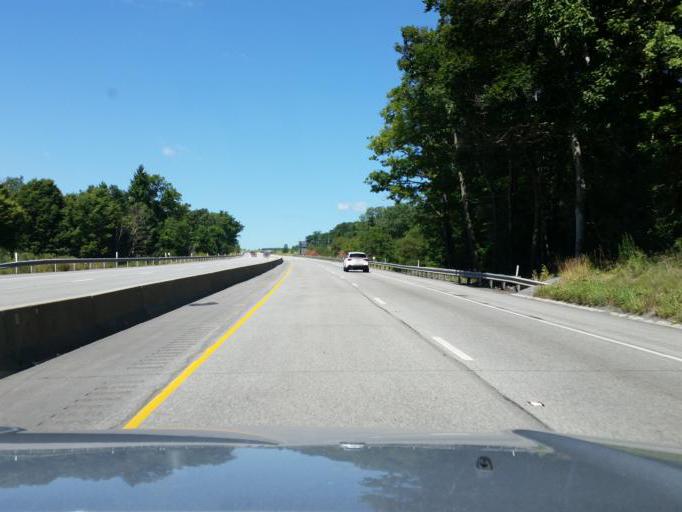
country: US
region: Pennsylvania
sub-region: Cambria County
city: Mundys Corner
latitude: 40.4508
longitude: -78.8480
